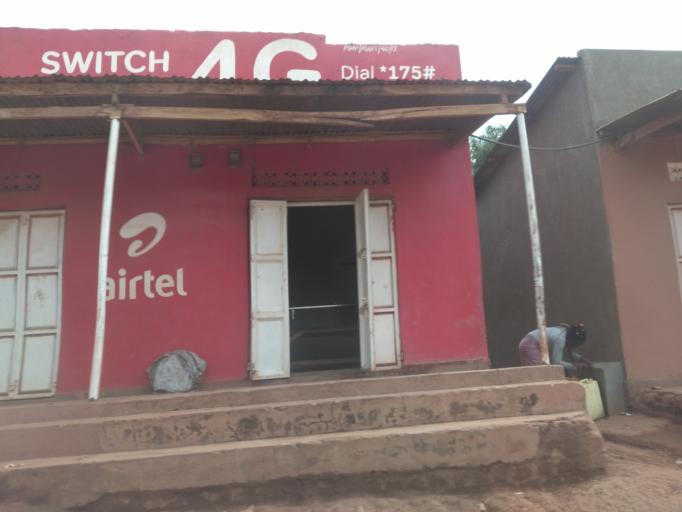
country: UG
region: Central Region
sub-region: Wakiso District
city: Bweyogerere
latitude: 0.4643
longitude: 32.6247
